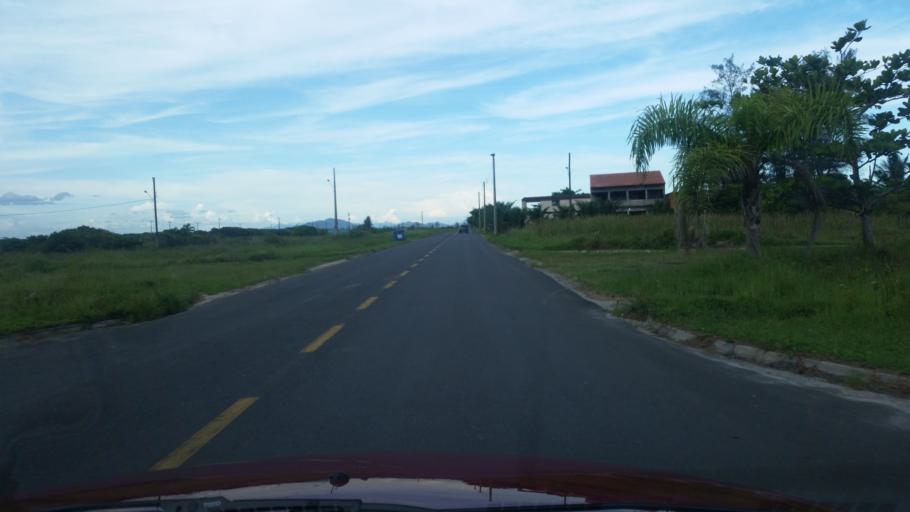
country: BR
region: Sao Paulo
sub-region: Iguape
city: Iguape
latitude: -24.8241
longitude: -47.6624
